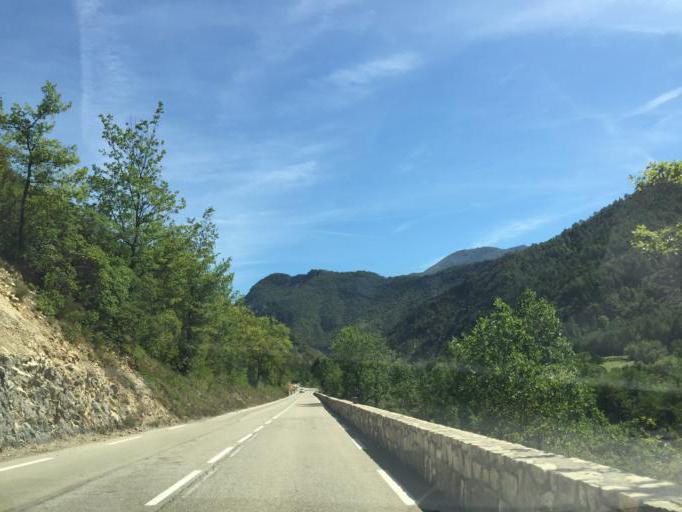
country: FR
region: Provence-Alpes-Cote d'Azur
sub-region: Departement des Alpes-Maritimes
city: Gilette
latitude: 43.9547
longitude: 7.1586
